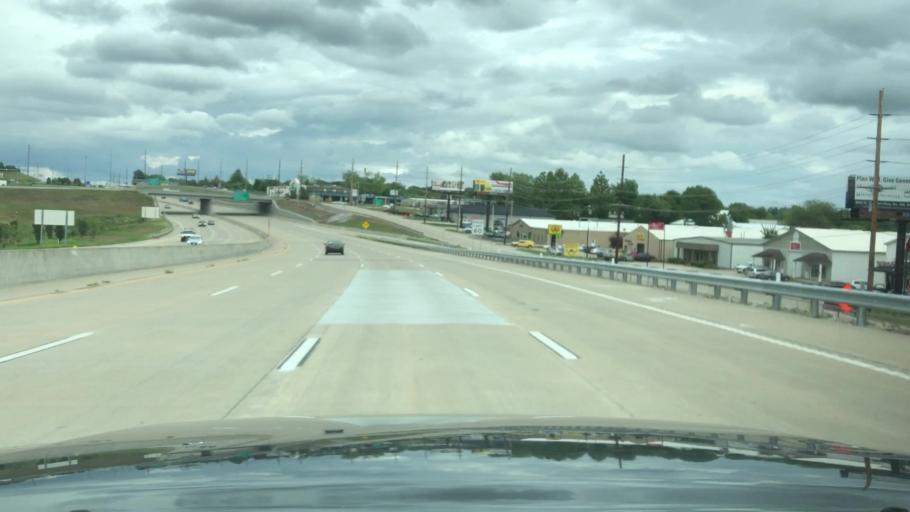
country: US
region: Missouri
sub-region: Saint Charles County
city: Cottleville
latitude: 38.7406
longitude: -90.6122
